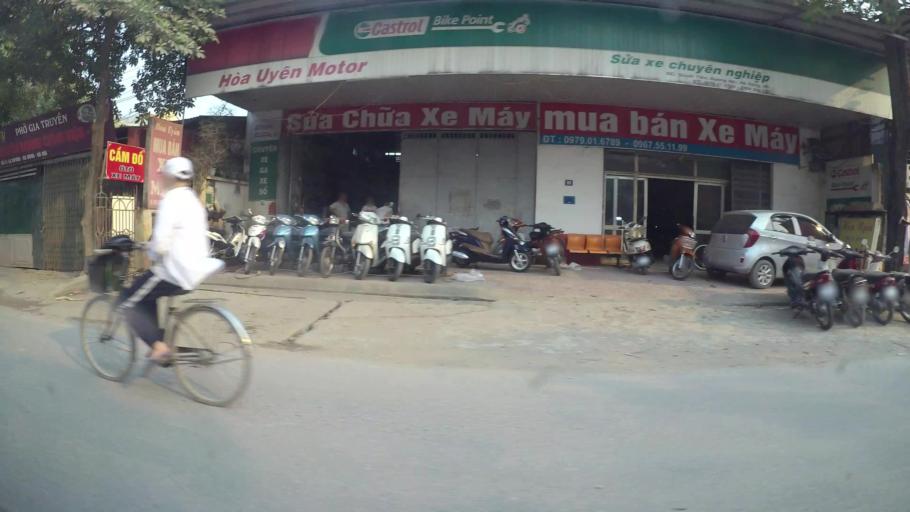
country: VN
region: Ha Noi
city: Ha Dong
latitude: 20.9942
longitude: 105.7391
